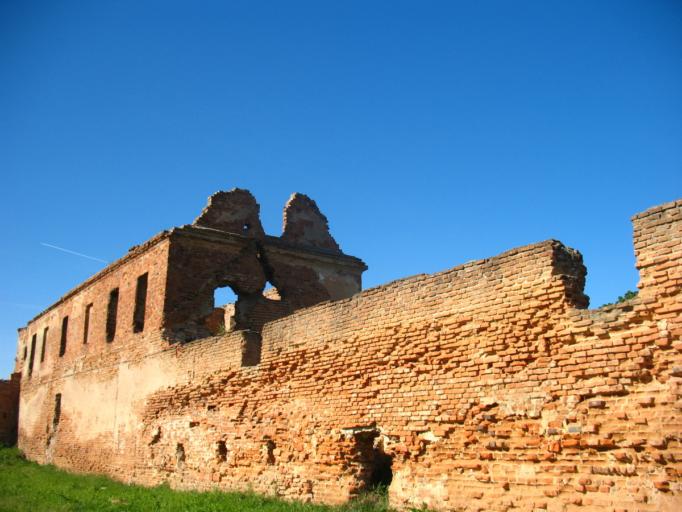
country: BY
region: Brest
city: Byaroza
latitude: 52.5329
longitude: 24.9583
